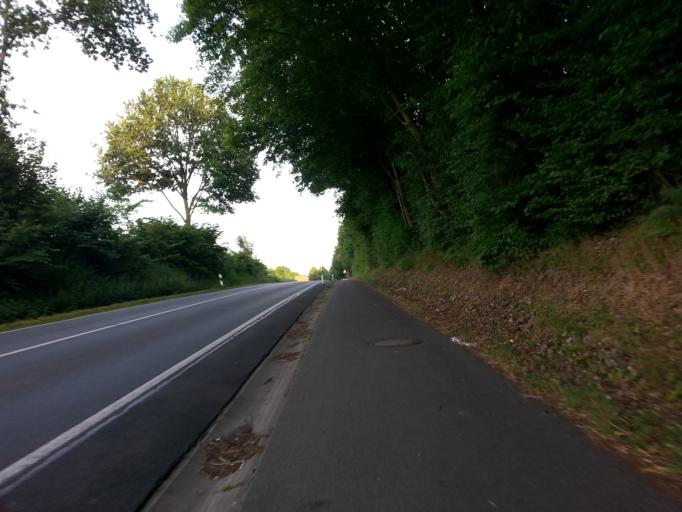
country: DE
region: North Rhine-Westphalia
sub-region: Regierungsbezirk Munster
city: Havixbeck
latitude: 51.9654
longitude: 7.4128
